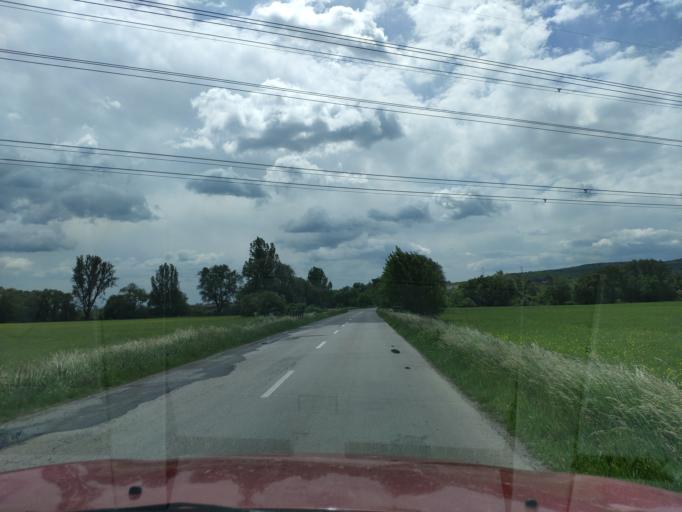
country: SK
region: Presovsky
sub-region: Okres Presov
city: Presov
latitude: 48.8612
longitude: 21.2708
